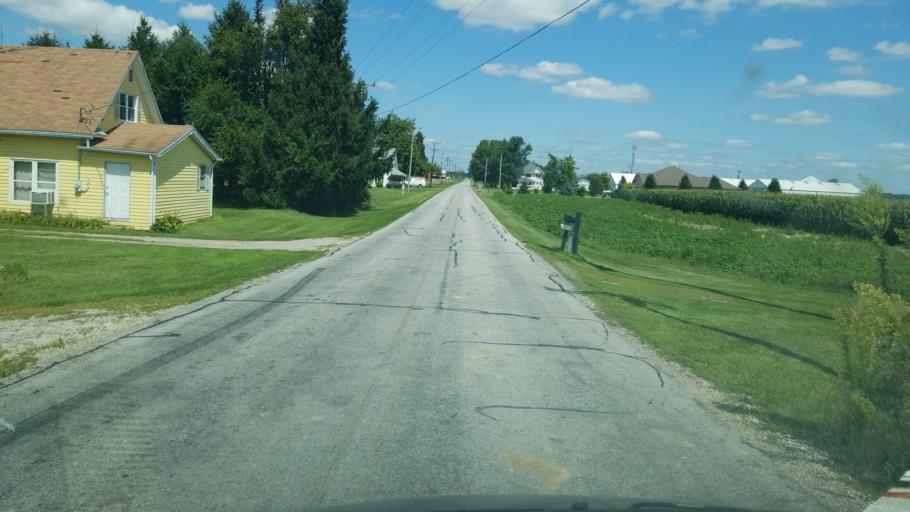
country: US
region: Ohio
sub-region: Fulton County
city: Swanton
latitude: 41.5800
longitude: -83.9407
